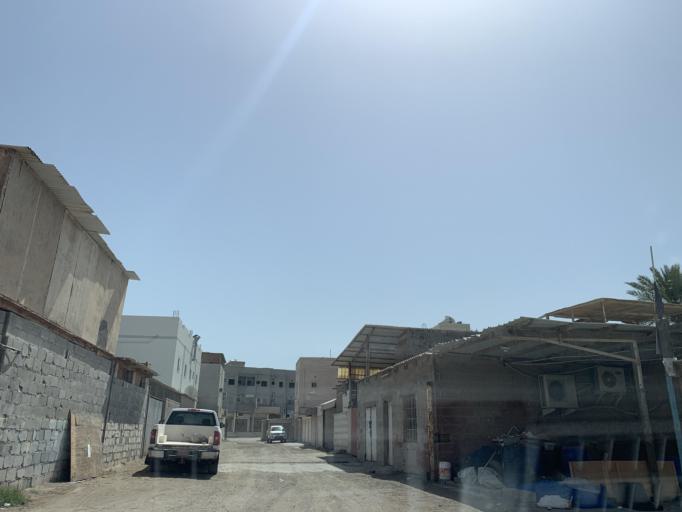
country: BH
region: Northern
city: Sitrah
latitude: 26.1452
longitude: 50.6066
